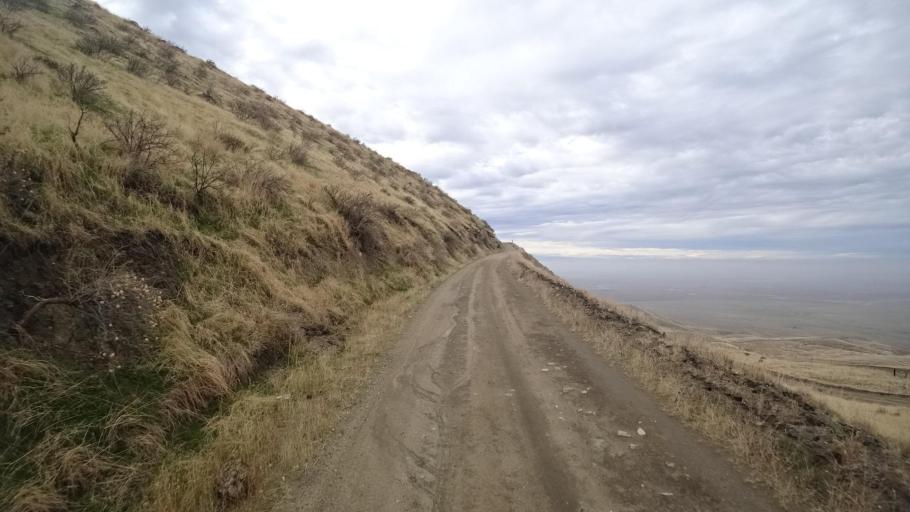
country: US
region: California
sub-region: Kern County
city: Arvin
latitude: 35.1386
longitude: -118.7790
